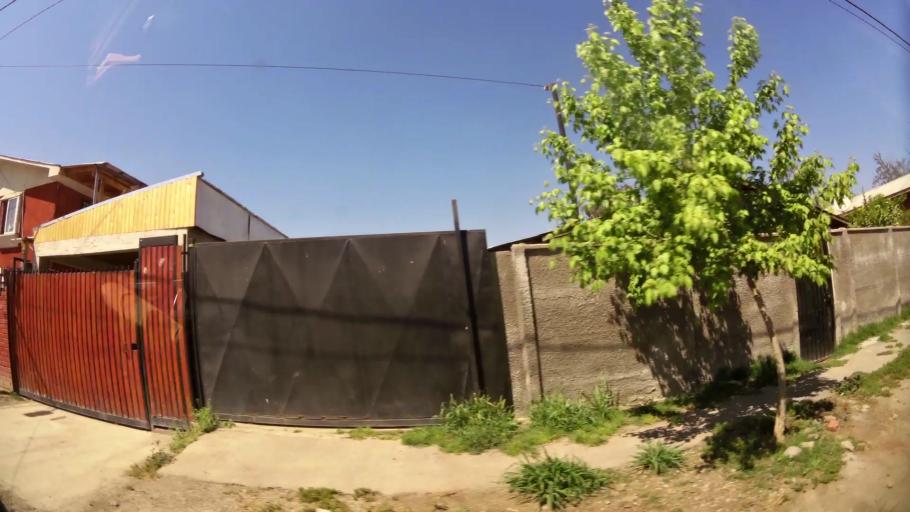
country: CL
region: Santiago Metropolitan
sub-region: Provincia de Talagante
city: Penaflor
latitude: -33.5940
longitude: -70.8124
